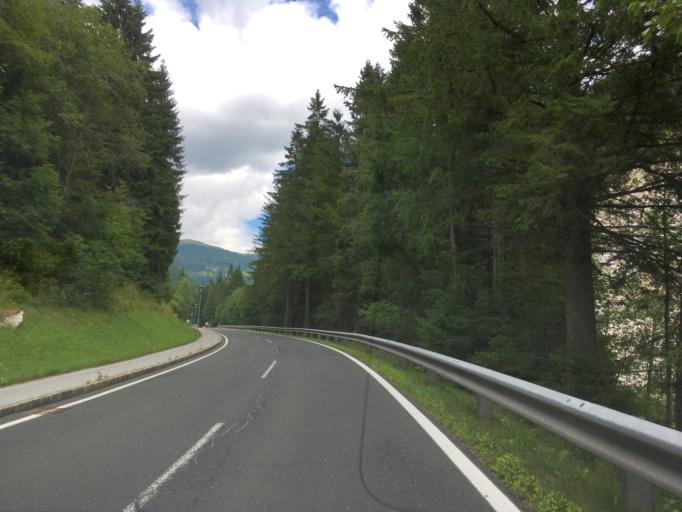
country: AT
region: Carinthia
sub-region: Politischer Bezirk Spittal an der Drau
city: Kleinkirchheim
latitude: 46.8290
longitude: 13.7692
